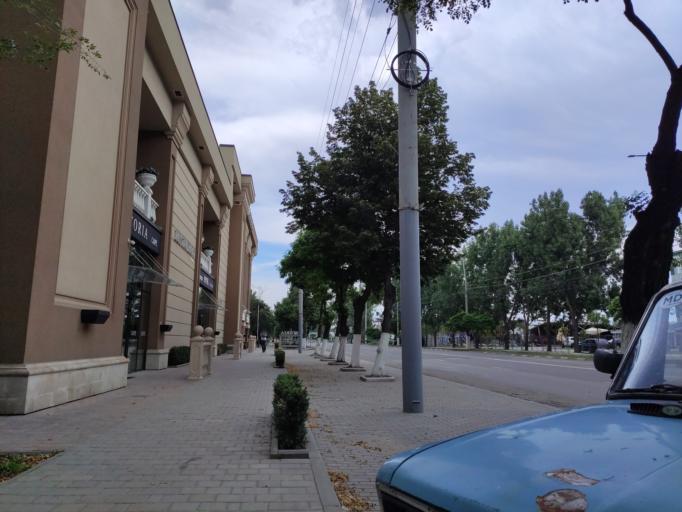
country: MD
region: Balti
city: Balti
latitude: 47.7598
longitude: 27.9407
